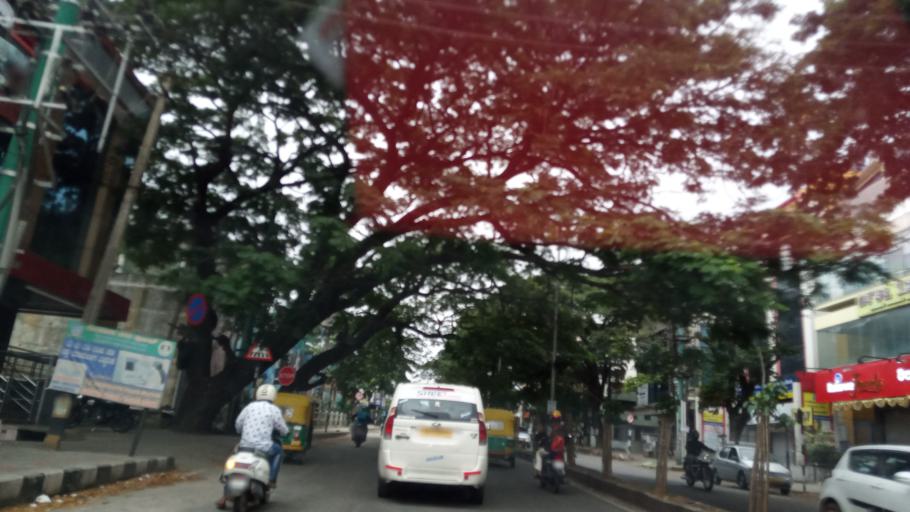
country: IN
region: Karnataka
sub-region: Bangalore Urban
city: Bangalore
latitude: 12.9230
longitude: 77.5562
